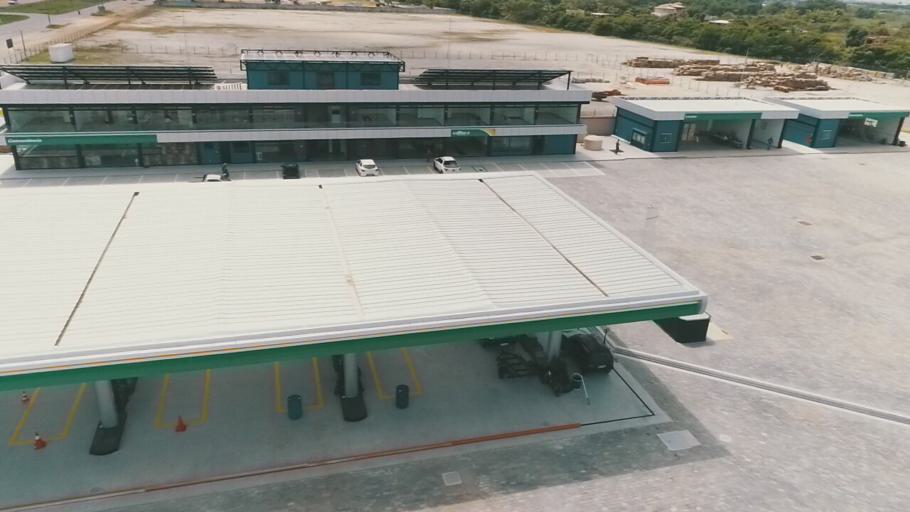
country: BR
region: Rio de Janeiro
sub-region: Macae
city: Macae
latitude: -22.3466
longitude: -41.7920
